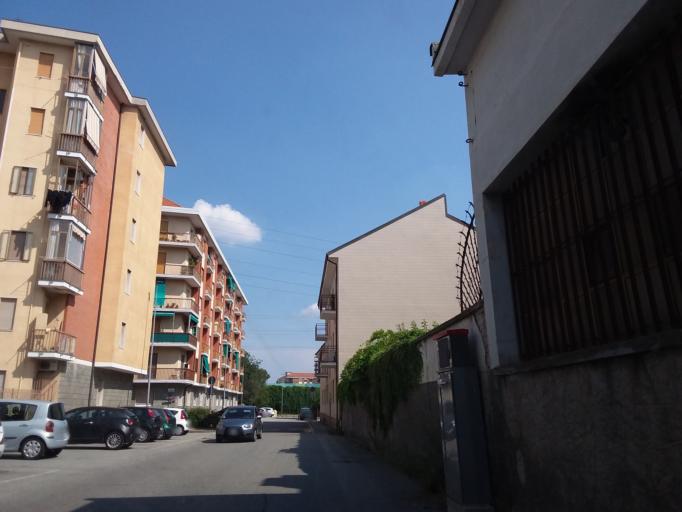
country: IT
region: Piedmont
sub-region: Provincia di Torino
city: Rivoli
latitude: 45.0734
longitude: 7.5443
